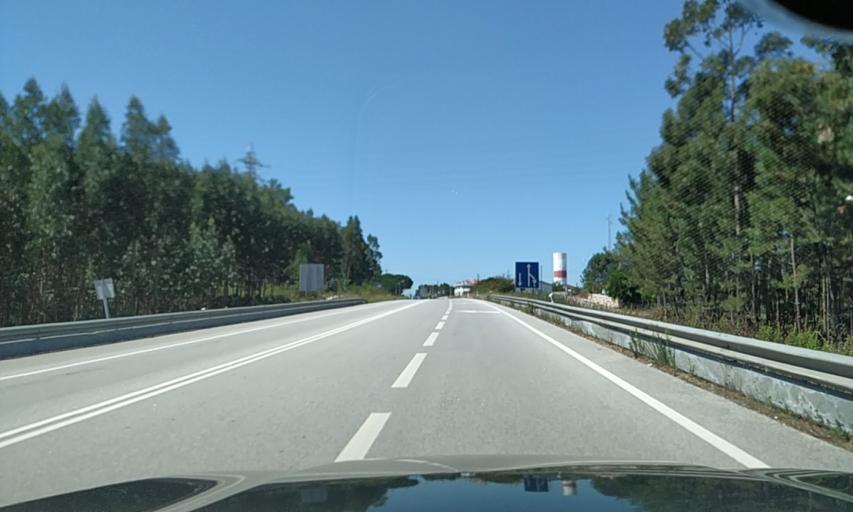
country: PT
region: Aveiro
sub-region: Agueda
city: Agueda
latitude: 40.5574
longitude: -8.4613
